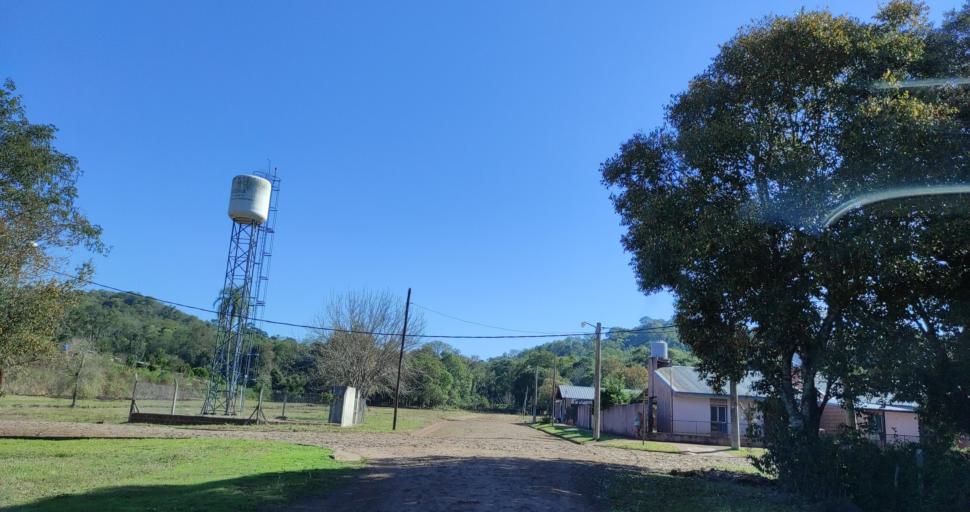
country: AR
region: Misiones
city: Cerro Cora
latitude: -27.6278
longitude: -55.7048
